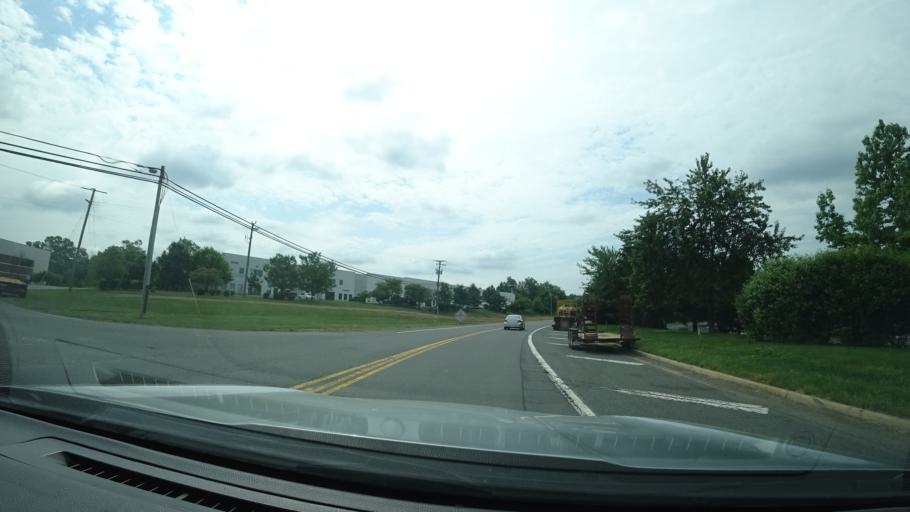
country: US
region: Virginia
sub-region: Loudoun County
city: Oak Grove
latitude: 38.9849
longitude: -77.4230
